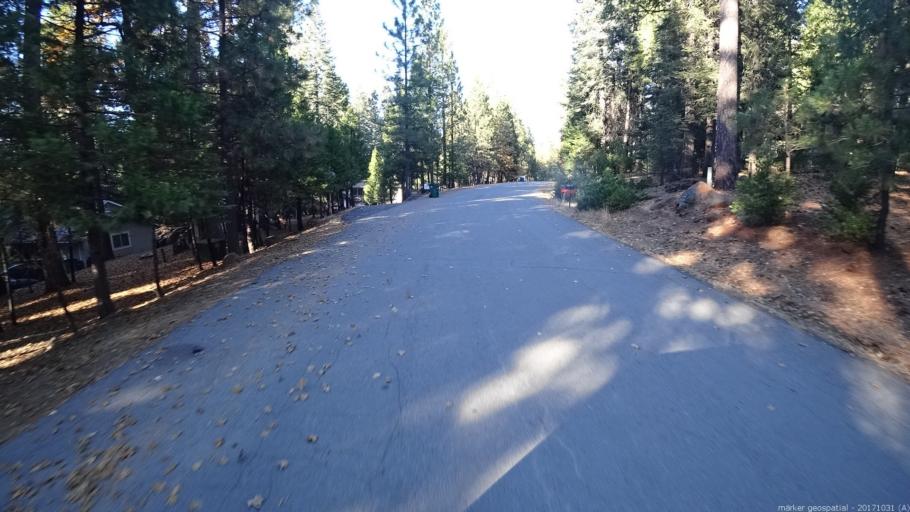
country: US
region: California
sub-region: Shasta County
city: Shingletown
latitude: 40.4984
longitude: -121.9041
